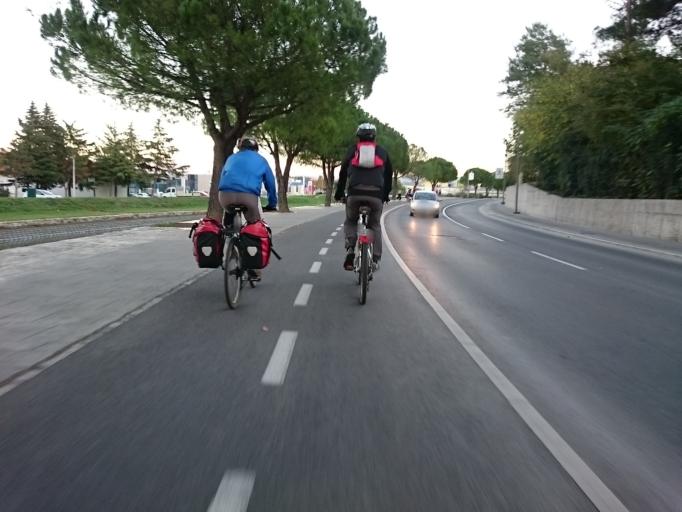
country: SI
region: Koper-Capodistria
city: Koper
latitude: 45.5391
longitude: 13.7248
